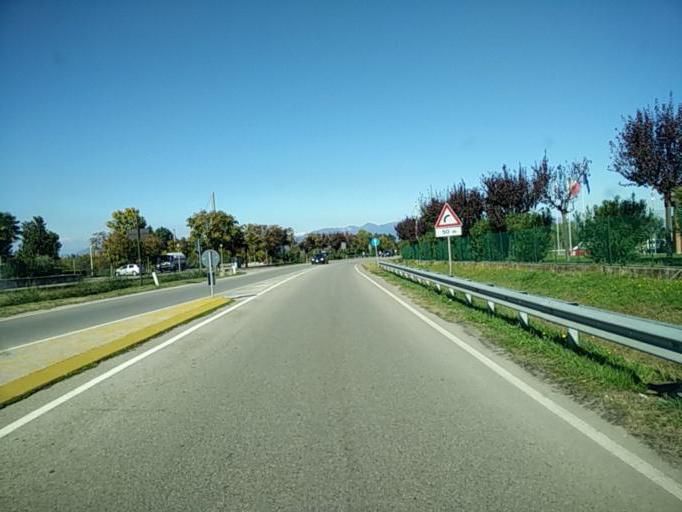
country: IT
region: Lombardy
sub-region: Provincia di Brescia
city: San Martino della Battaglia
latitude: 45.4479
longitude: 10.5944
